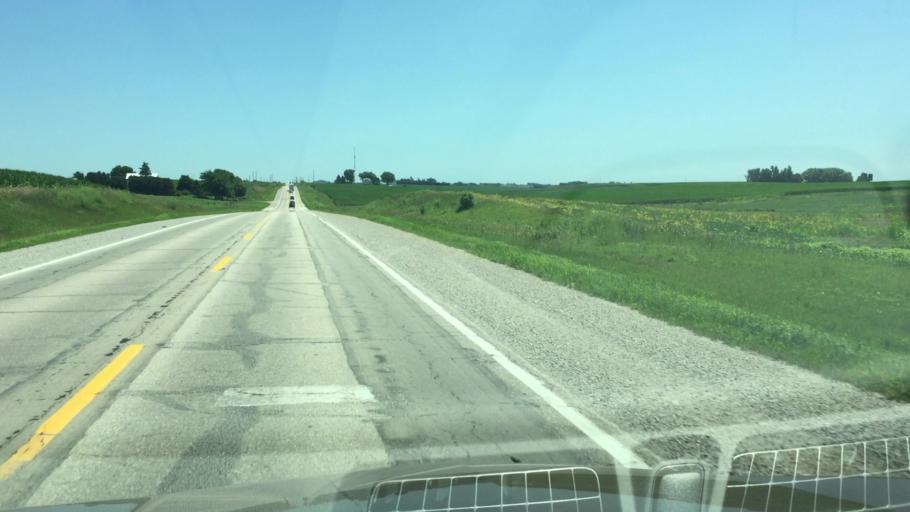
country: US
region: Iowa
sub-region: Cedar County
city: Mechanicsville
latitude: 41.8887
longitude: -91.2045
